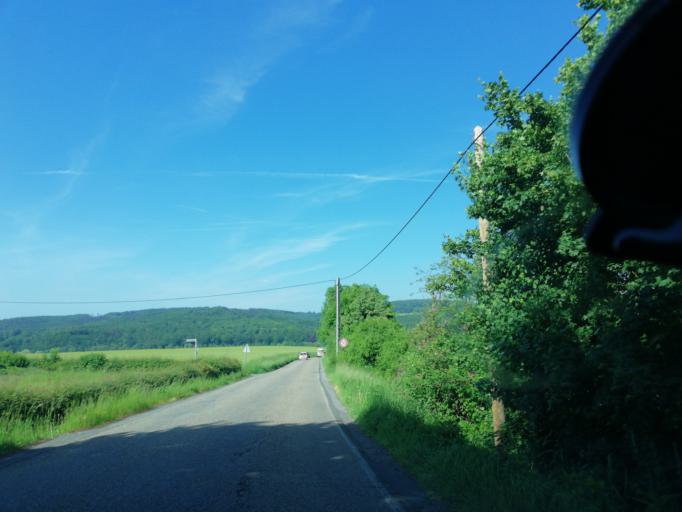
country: DE
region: North Rhine-Westphalia
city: Wetter (Ruhr)
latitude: 51.3864
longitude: 7.3595
